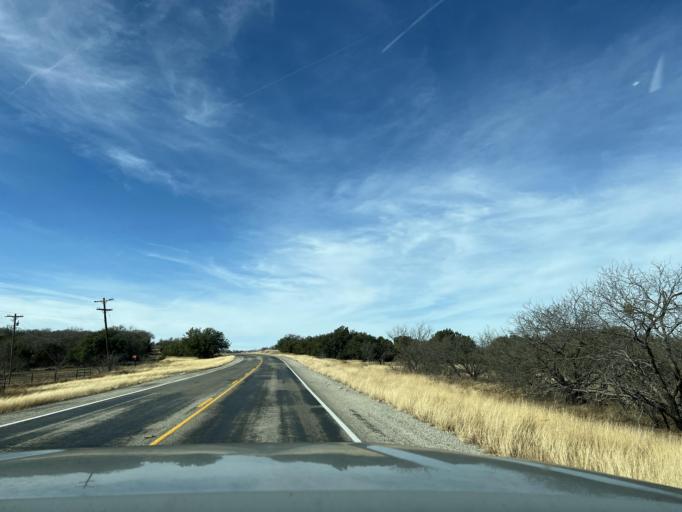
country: US
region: Texas
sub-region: Eastland County
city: Cisco
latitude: 32.4570
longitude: -98.9893
